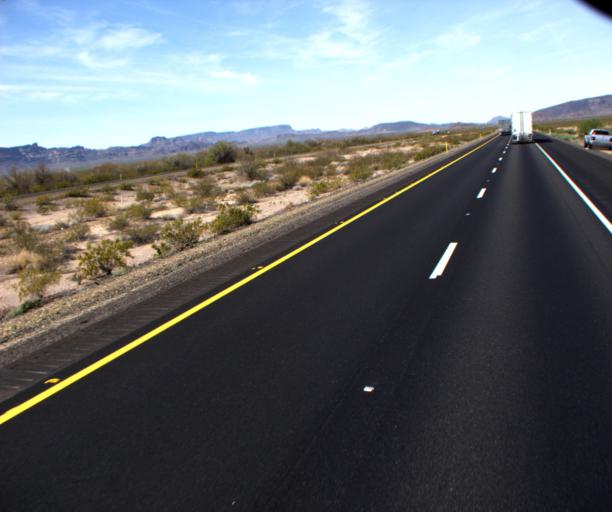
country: US
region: Arizona
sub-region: La Paz County
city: Salome
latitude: 33.6386
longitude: -113.8170
